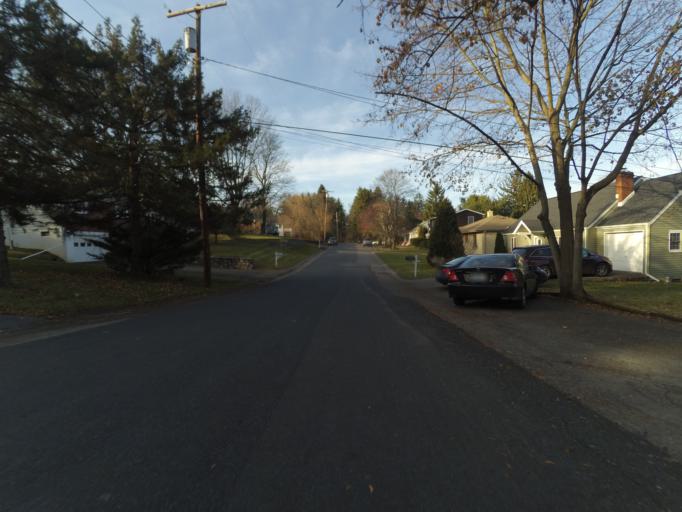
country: US
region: Pennsylvania
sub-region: Centre County
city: Lemont
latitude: 40.8047
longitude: -77.8216
